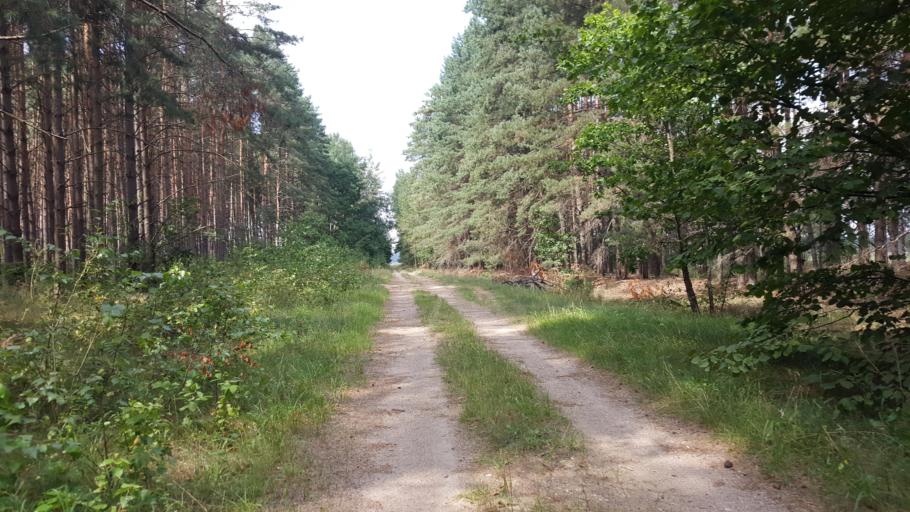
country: PL
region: Podlasie
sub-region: Powiat hajnowski
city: Hajnowka
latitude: 52.5729
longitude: 23.5885
